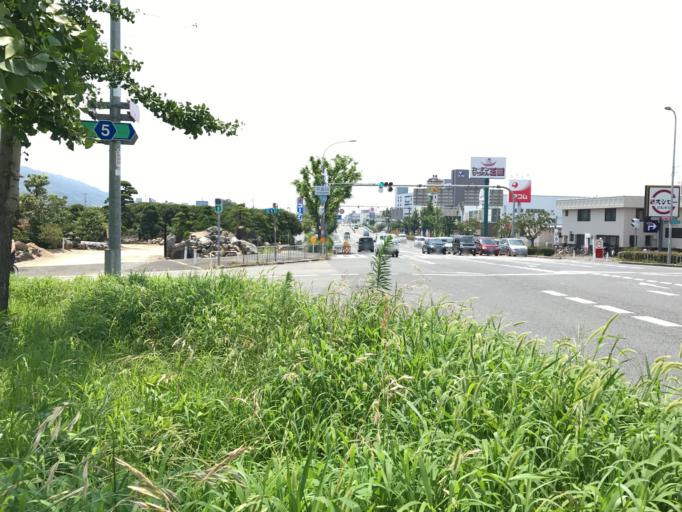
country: JP
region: Osaka
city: Yao
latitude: 34.6263
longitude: 135.6323
